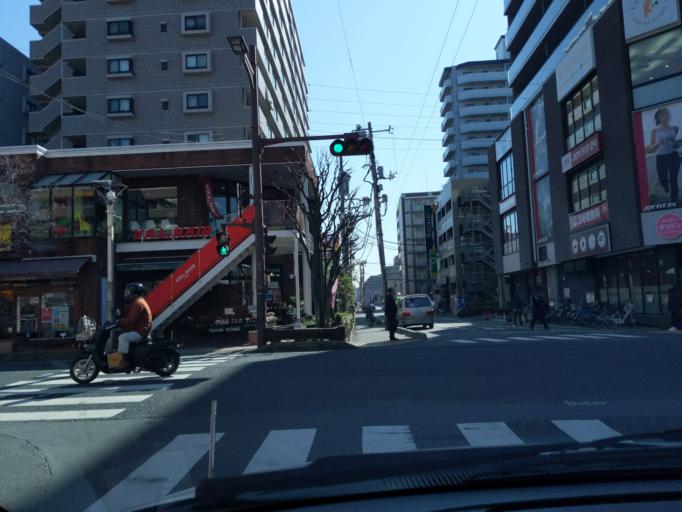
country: JP
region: Saitama
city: Soka
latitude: 35.8442
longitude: 139.8025
